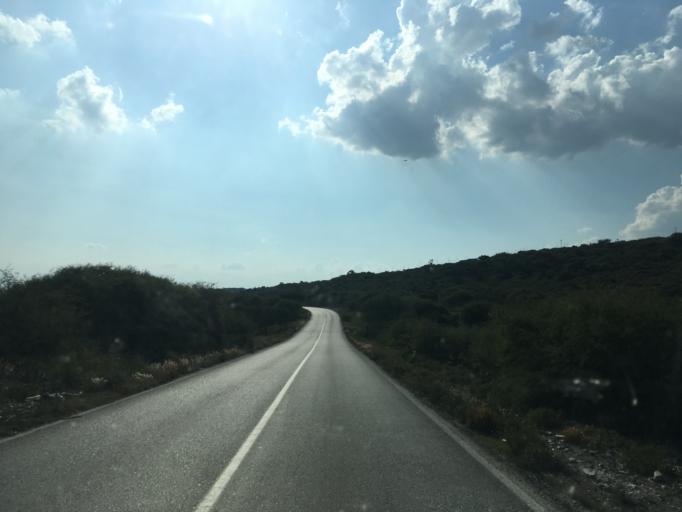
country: MX
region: Hidalgo
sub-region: Cardonal
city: Pozuelos
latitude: 20.6001
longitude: -99.1136
